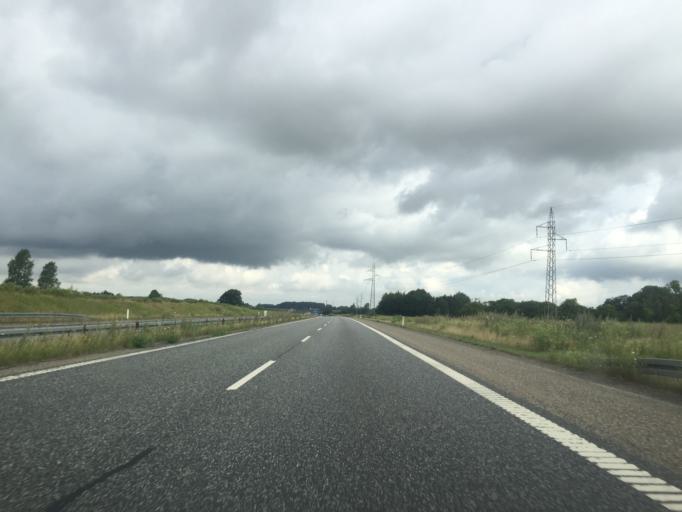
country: DK
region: South Denmark
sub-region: Faaborg-Midtfyn Kommune
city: Ringe
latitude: 55.1743
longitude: 10.5396
